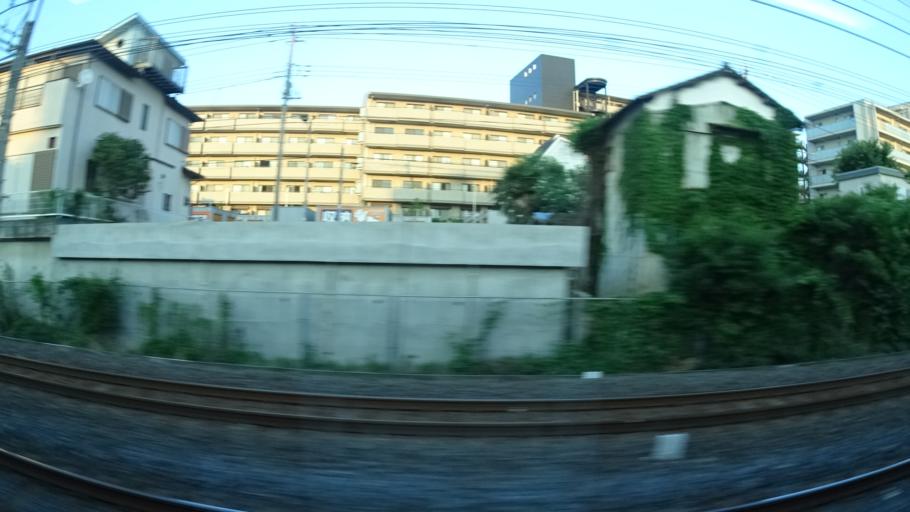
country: JP
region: Chiba
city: Matsudo
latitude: 35.8189
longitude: 139.9190
